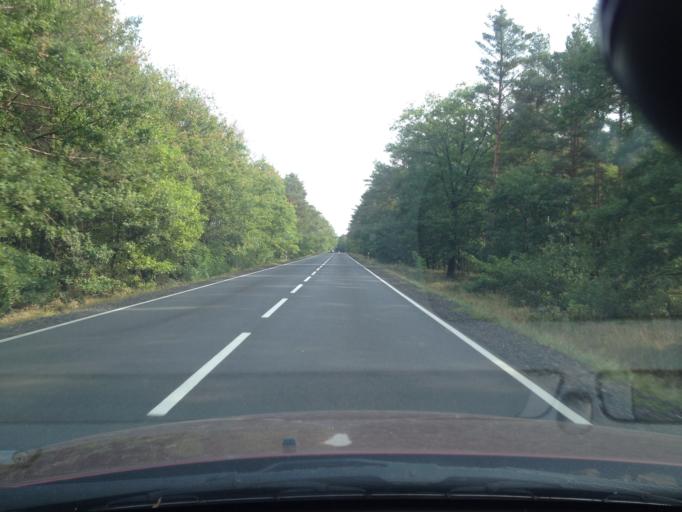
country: PL
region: Lubusz
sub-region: Powiat zaganski
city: Szprotawa
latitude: 51.4536
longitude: 15.6084
